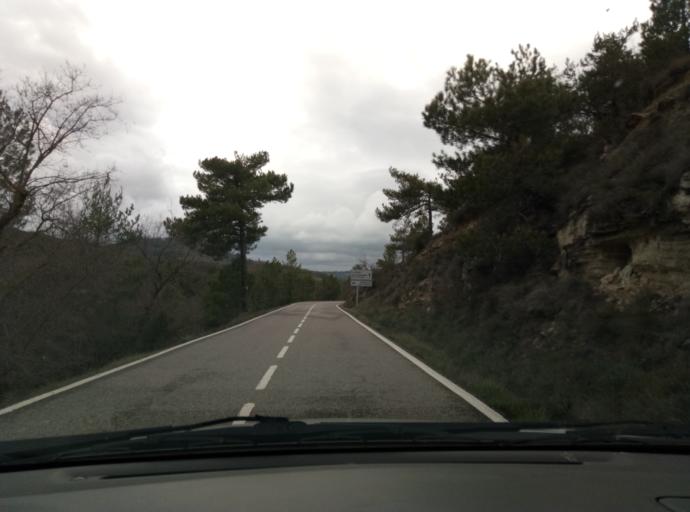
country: ES
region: Catalonia
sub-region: Provincia de Tarragona
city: Conesa
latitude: 41.5437
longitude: 1.3270
